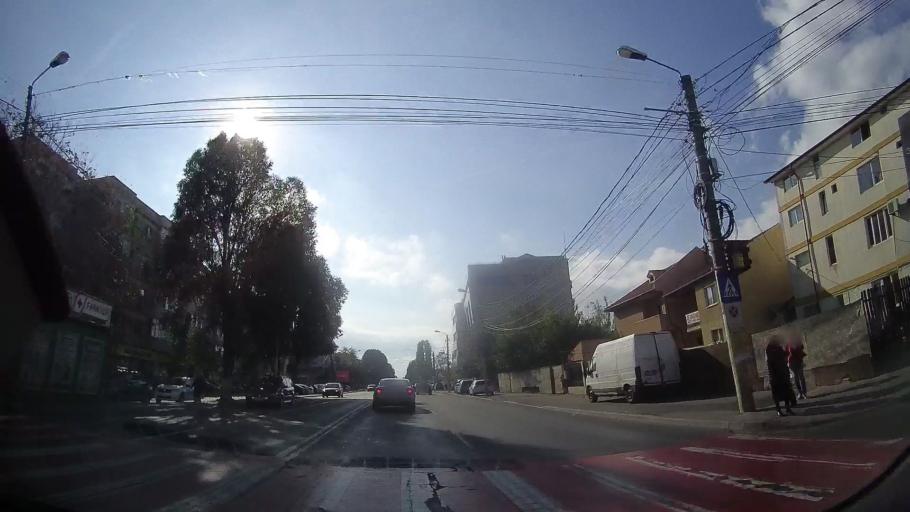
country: RO
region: Constanta
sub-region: Municipiul Constanta
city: Constanta
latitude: 44.1416
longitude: 28.6225
